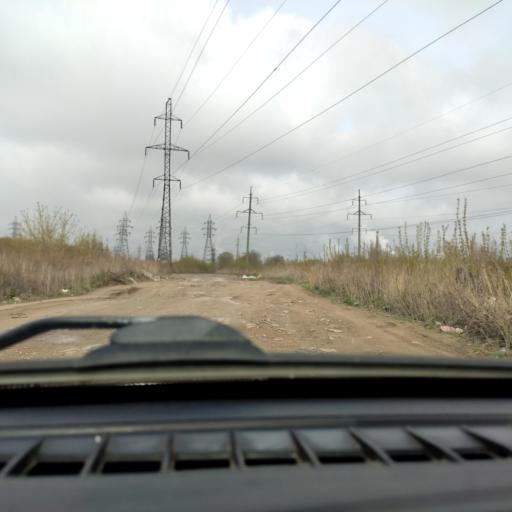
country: RU
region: Samara
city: Zhigulevsk
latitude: 53.5385
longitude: 49.4992
